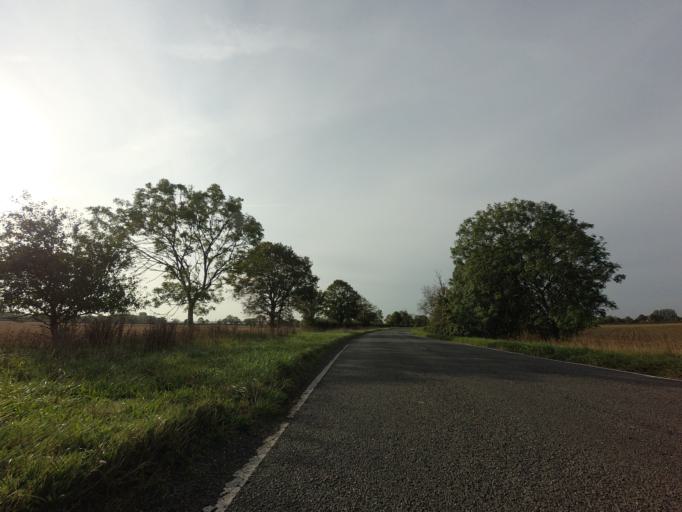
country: GB
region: England
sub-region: Cambridgeshire
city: Harston
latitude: 52.1007
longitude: 0.0838
